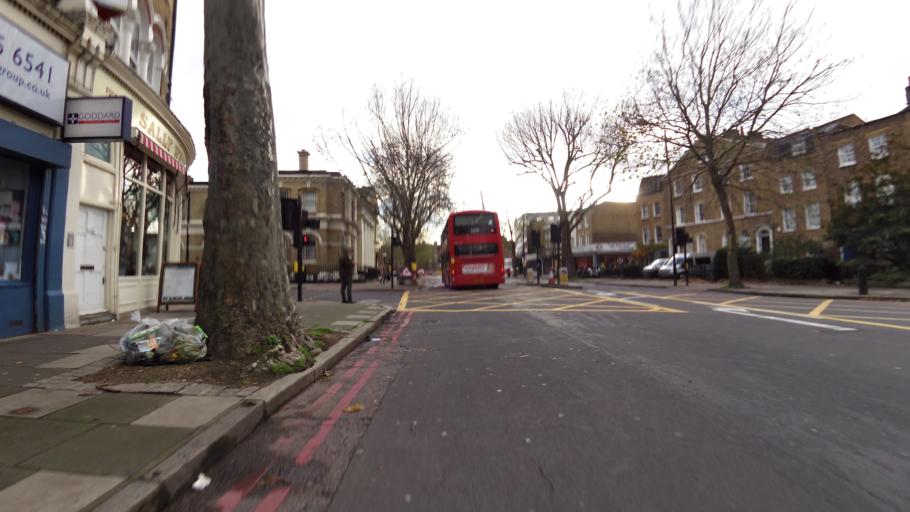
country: GB
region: England
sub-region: Greater London
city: Kennington
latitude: 51.4872
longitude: -0.1113
